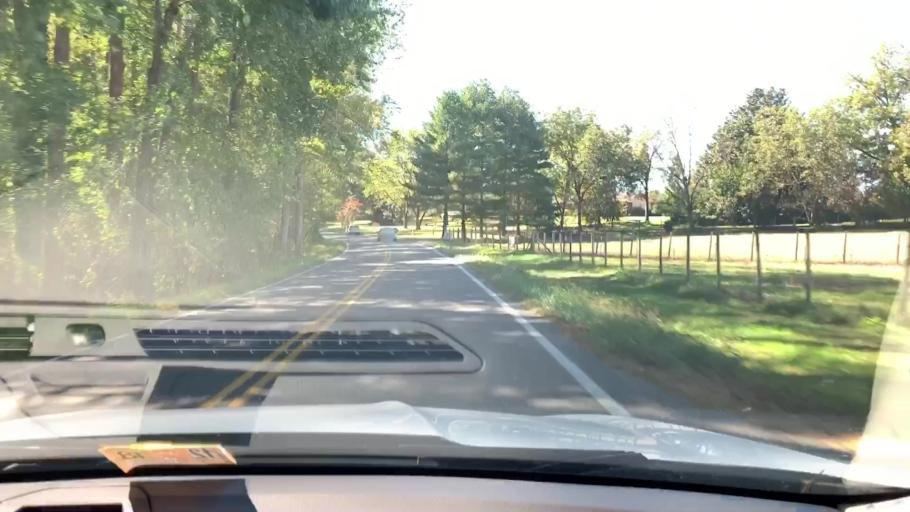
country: US
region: Virginia
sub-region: King William County
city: West Point
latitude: 37.4675
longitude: -76.8347
